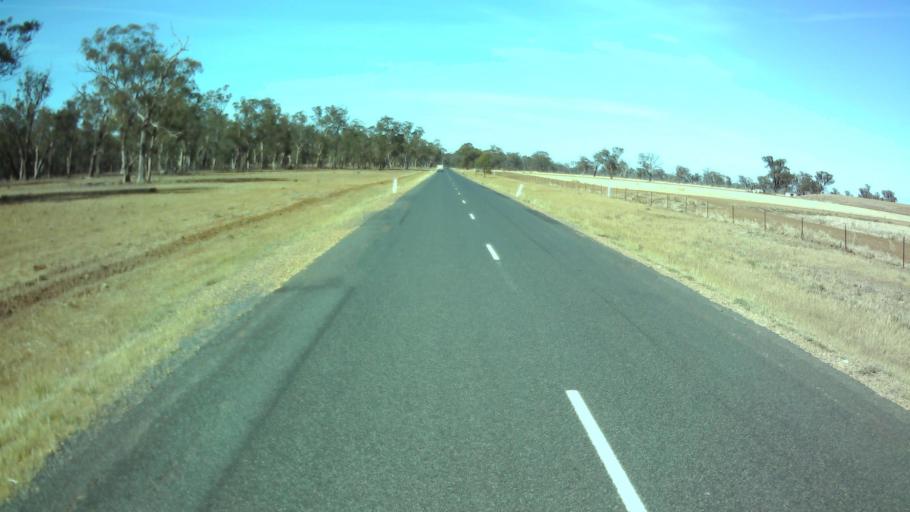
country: AU
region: New South Wales
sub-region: Weddin
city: Grenfell
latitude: -34.1290
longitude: 147.7984
